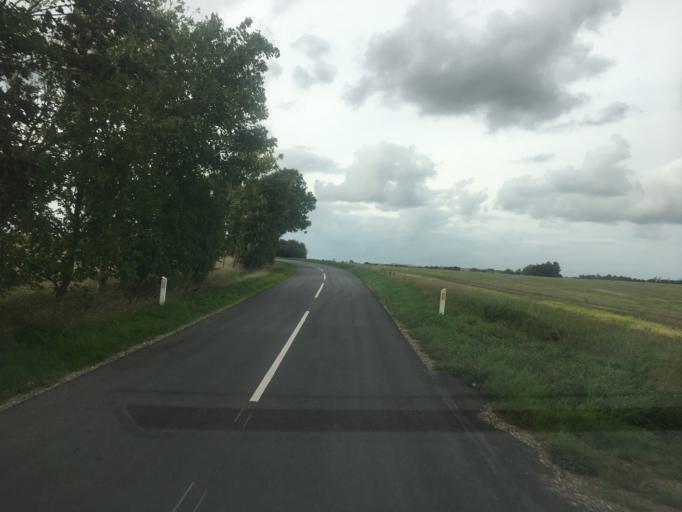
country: DE
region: Schleswig-Holstein
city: Aventoft
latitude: 54.9618
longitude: 8.8027
